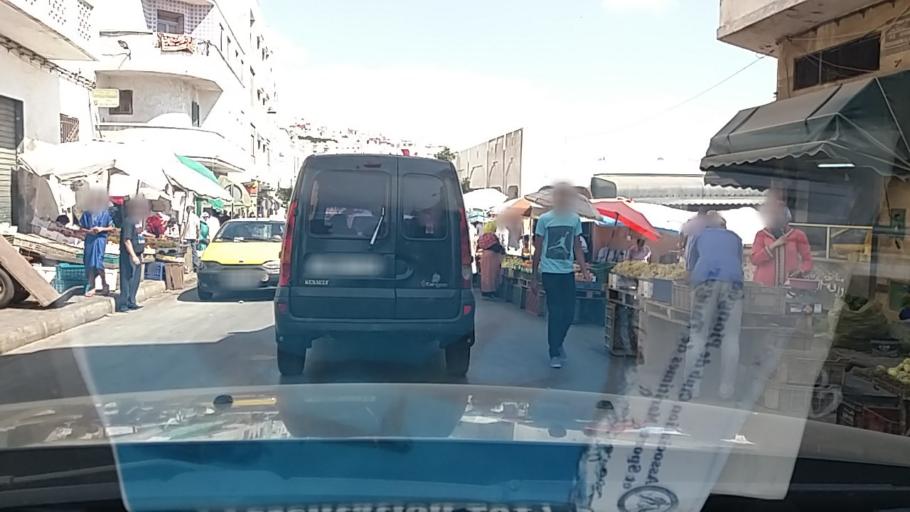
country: MA
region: Tanger-Tetouan
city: Tetouan
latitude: 35.5743
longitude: -5.3853
